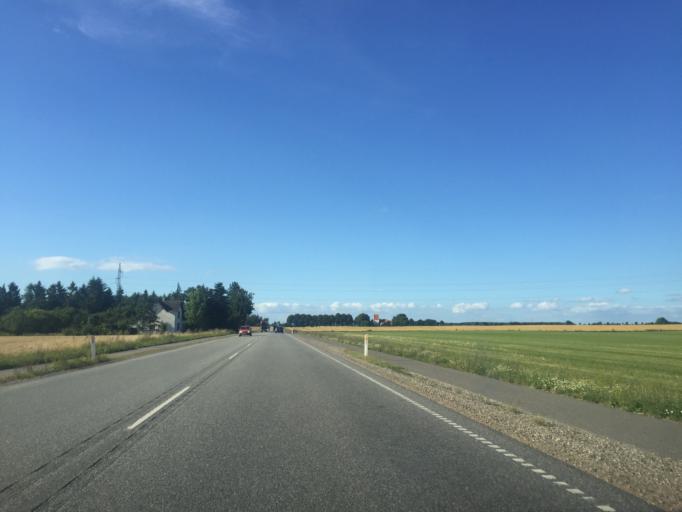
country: DK
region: Zealand
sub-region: Guldborgsund Kommune
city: Norre Alslev
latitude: 54.8405
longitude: 11.8589
